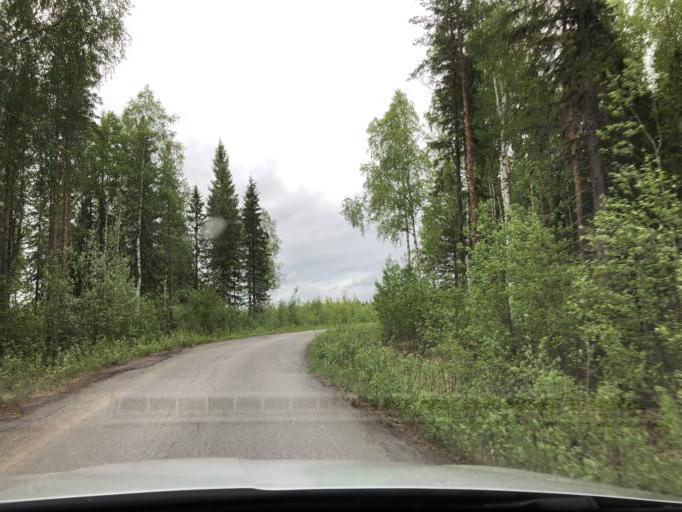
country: SE
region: Norrbotten
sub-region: Pitea Kommun
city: Roknas
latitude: 65.3849
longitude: 21.2672
